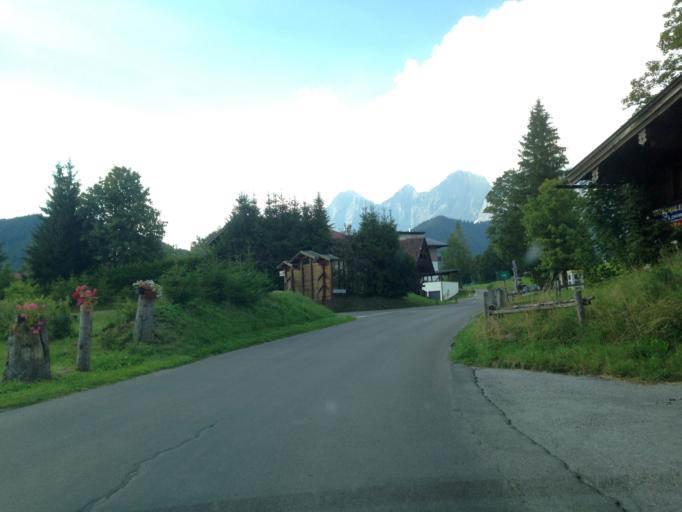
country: AT
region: Styria
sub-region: Politischer Bezirk Liezen
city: Schladming
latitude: 47.4079
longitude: 13.6365
